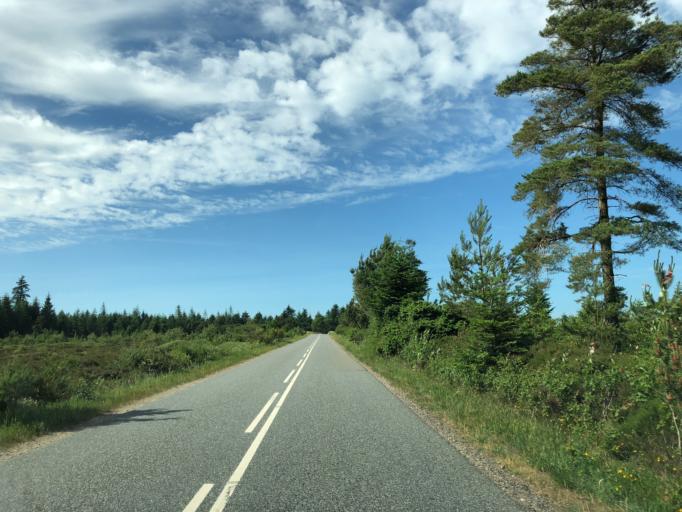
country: DK
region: Central Jutland
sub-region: Herning Kommune
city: Kibaek
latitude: 56.0613
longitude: 8.9181
